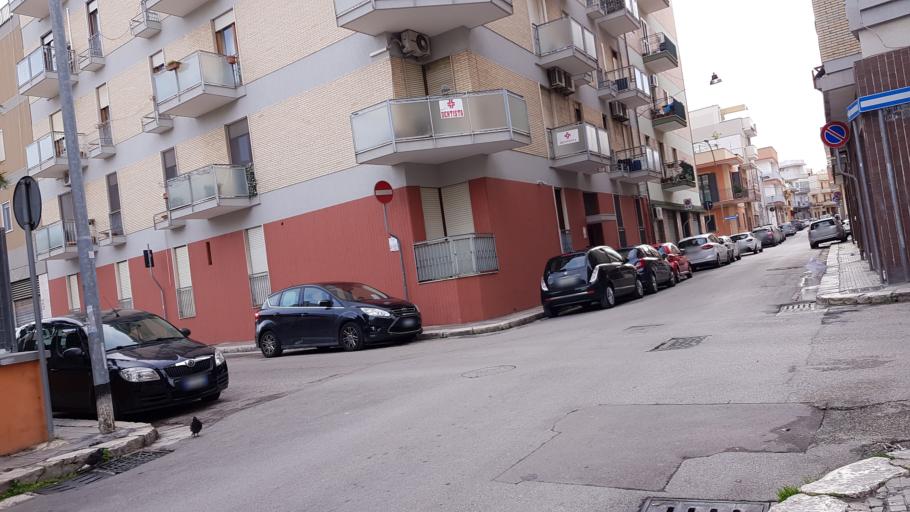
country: IT
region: Apulia
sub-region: Provincia di Brindisi
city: Brindisi
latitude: 40.6330
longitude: 17.9360
